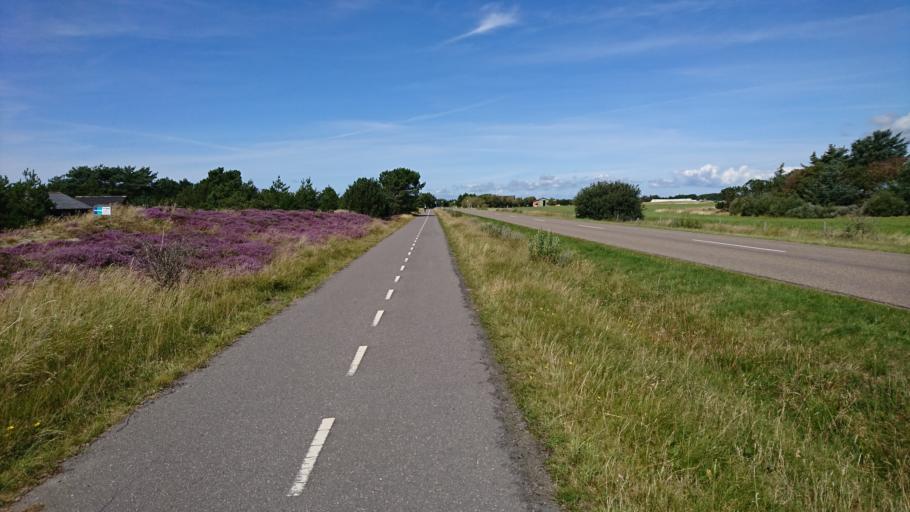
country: DK
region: South Denmark
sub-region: Fano Kommune
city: Nordby
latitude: 55.4155
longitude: 8.4031
